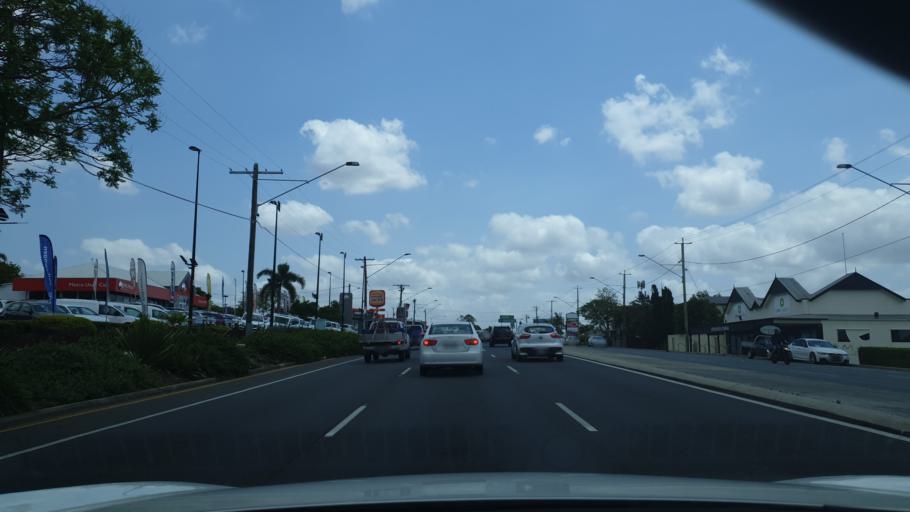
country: AU
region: Queensland
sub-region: Brisbane
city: Gordon Park
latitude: -27.4059
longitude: 153.0322
